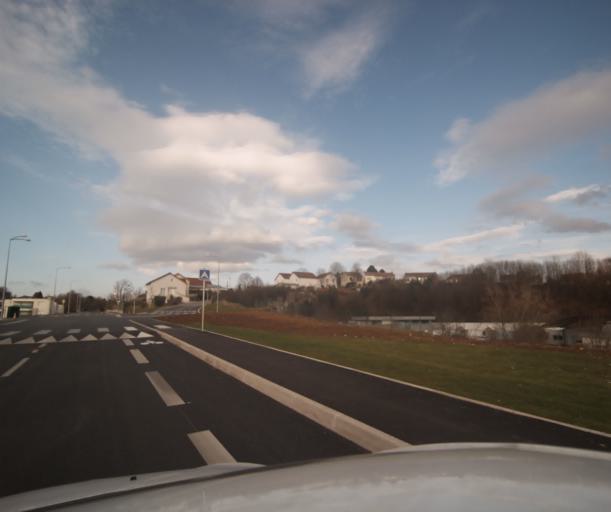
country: FR
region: Franche-Comte
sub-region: Departement du Doubs
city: Besancon
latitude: 47.2660
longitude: 6.0274
